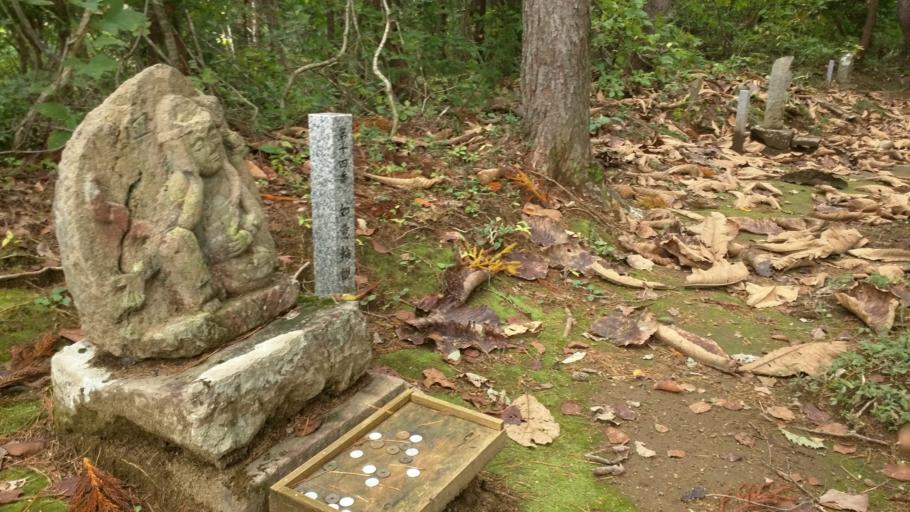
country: JP
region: Fukushima
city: Kitakata
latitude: 37.4589
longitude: 139.7275
